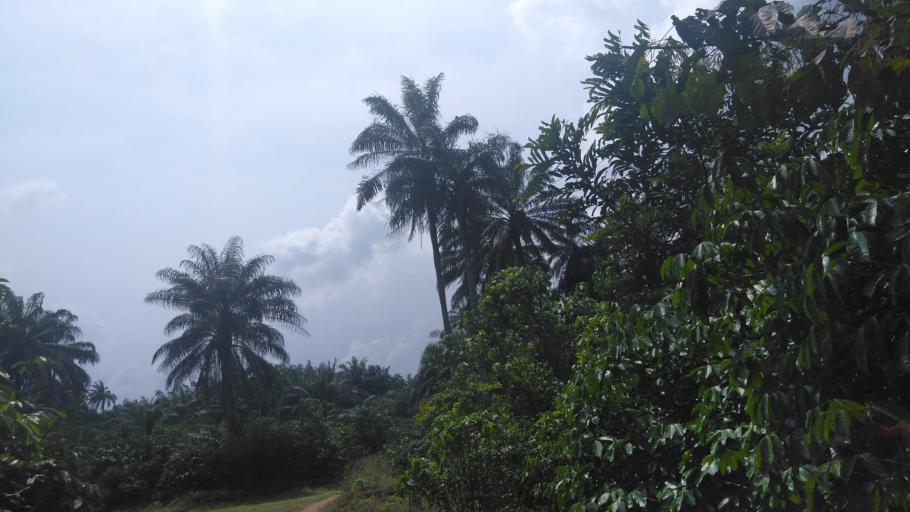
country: NG
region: Abia
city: Aba
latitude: 5.0439
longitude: 7.2388
